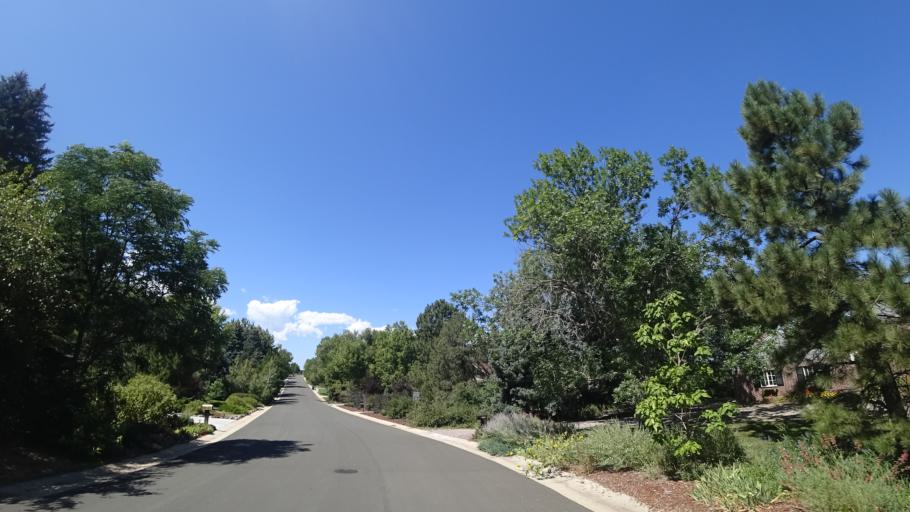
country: US
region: Colorado
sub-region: Arapahoe County
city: Cherry Hills Village
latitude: 39.6345
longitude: -104.9553
